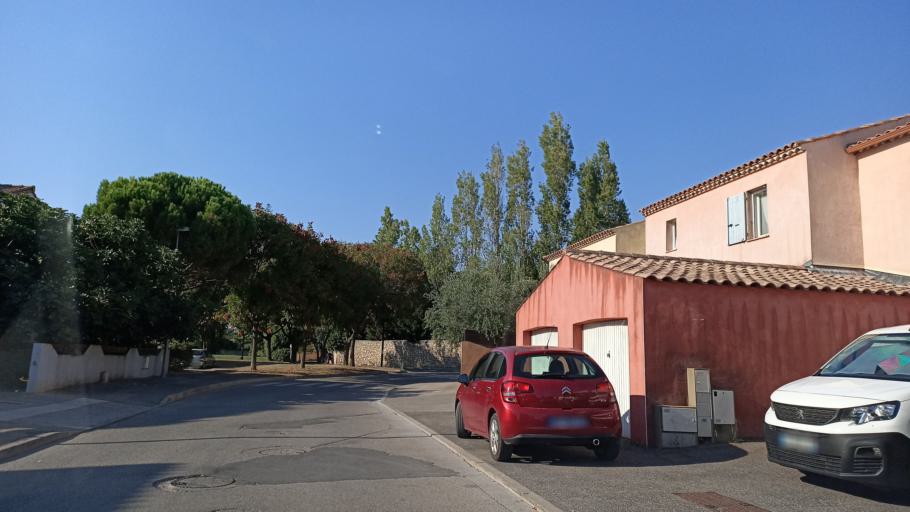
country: FR
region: Languedoc-Roussillon
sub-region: Departement de l'Herault
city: Lunel
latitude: 43.6866
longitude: 4.1292
